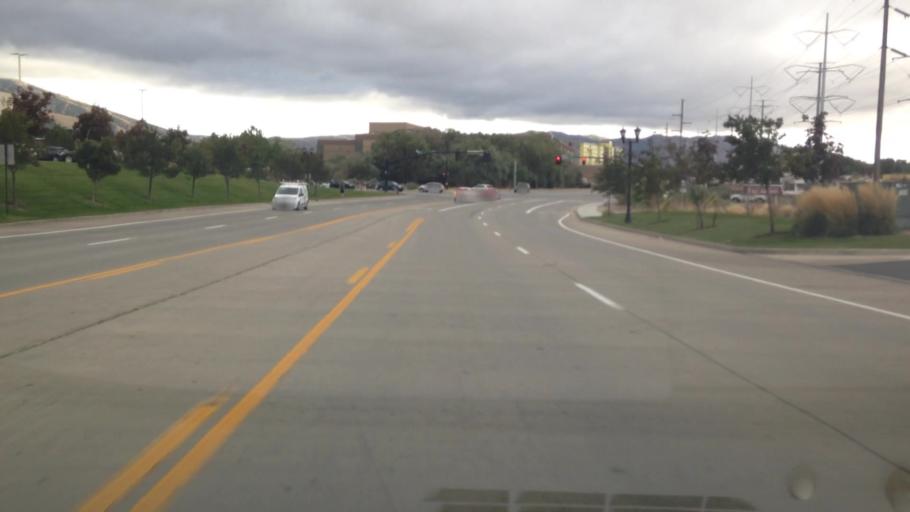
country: US
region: Utah
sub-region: Salt Lake County
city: South Jordan
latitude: 40.5709
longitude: -111.9050
